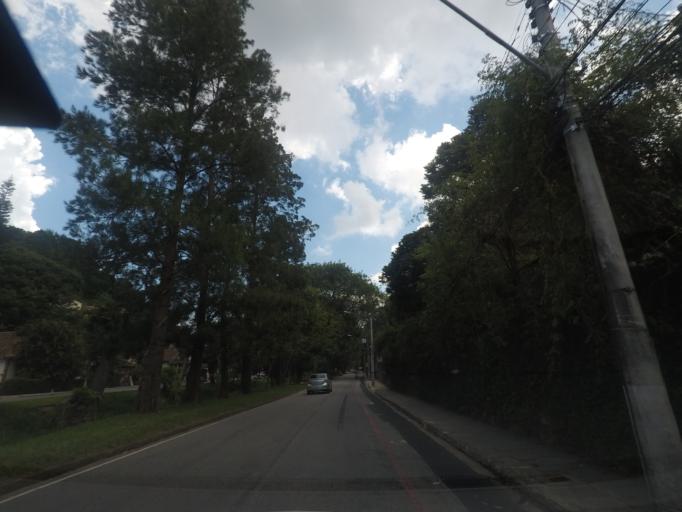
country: BR
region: Rio de Janeiro
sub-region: Petropolis
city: Petropolis
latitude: -22.5018
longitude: -43.1818
